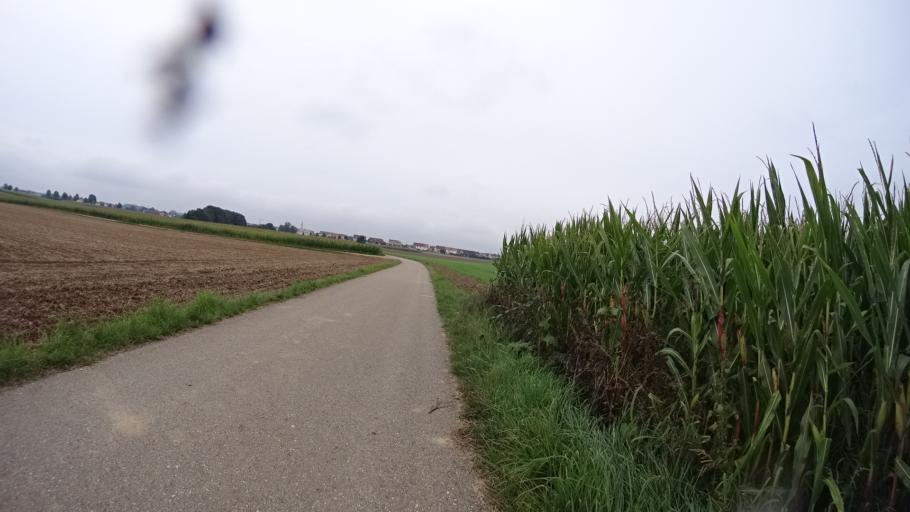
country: DE
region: Bavaria
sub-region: Upper Bavaria
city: Gaimersheim
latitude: 48.8211
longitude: 11.3639
